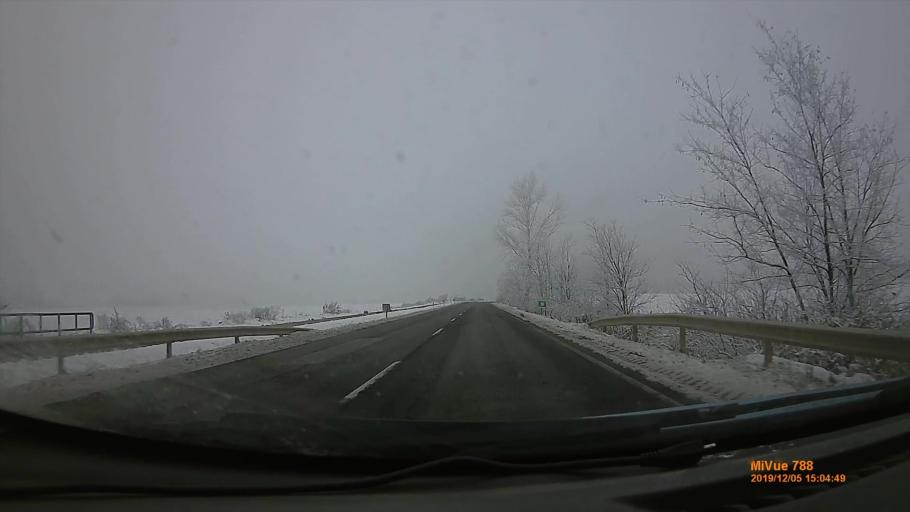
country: HU
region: Szabolcs-Szatmar-Bereg
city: Tiszanagyfalu
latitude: 48.1020
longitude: 21.4906
